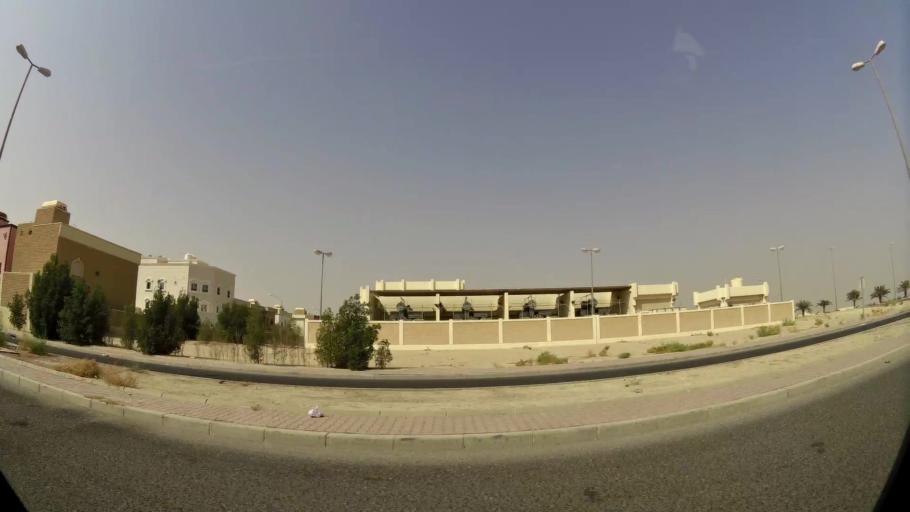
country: KW
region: Muhafazat al Jahra'
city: Al Jahra'
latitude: 29.3247
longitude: 47.7244
